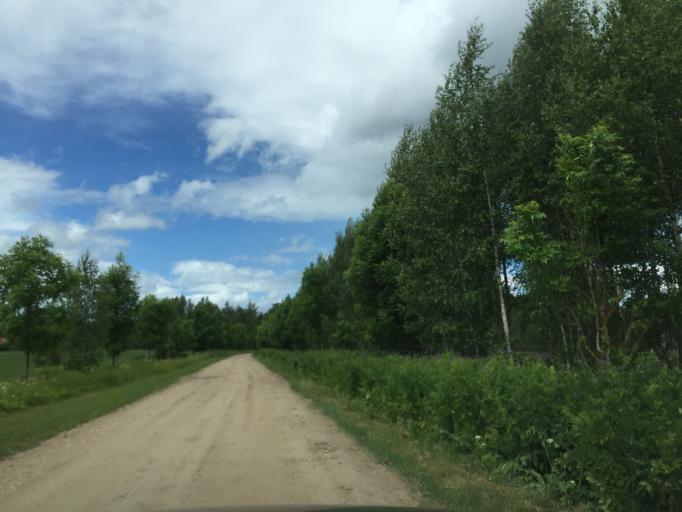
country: LV
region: Lecava
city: Iecava
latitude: 56.5731
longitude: 24.1142
